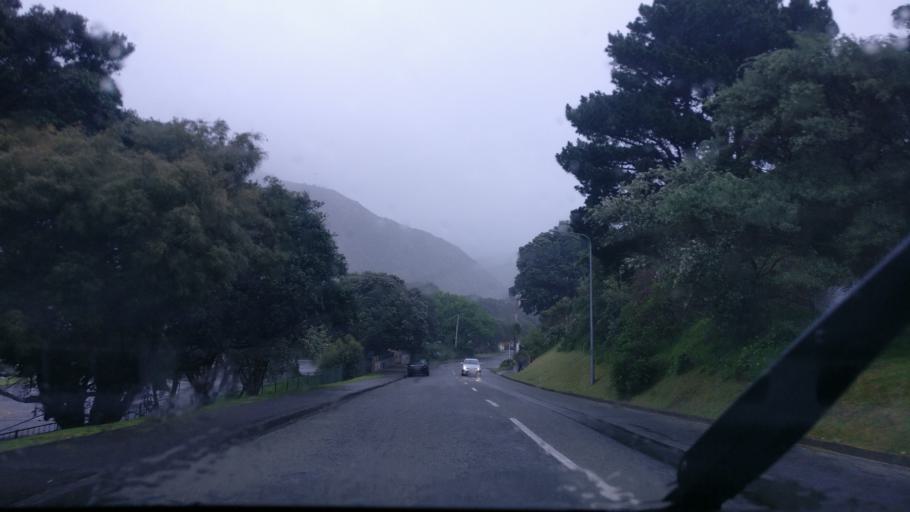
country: NZ
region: Wellington
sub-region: Kapiti Coast District
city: Paraparaumu
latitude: -40.9812
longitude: 174.9571
